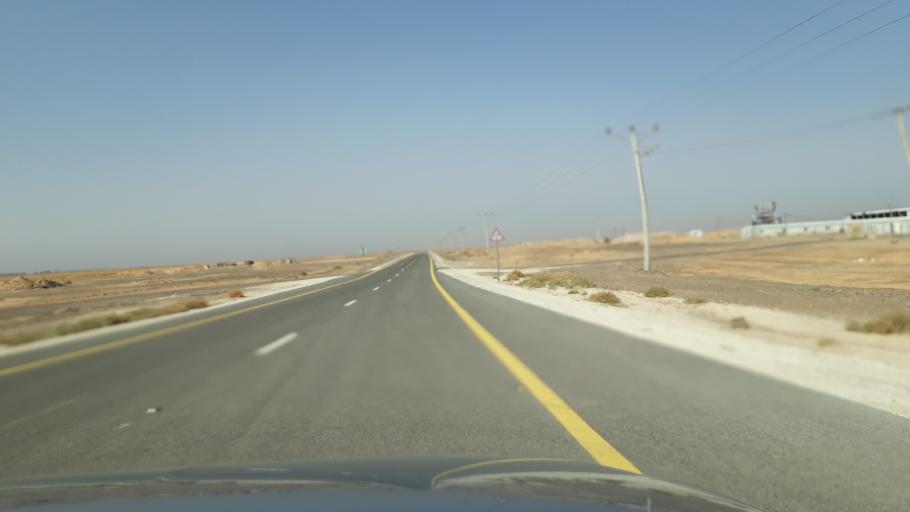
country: JO
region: Amman
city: Al Azraq ash Shamali
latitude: 31.7801
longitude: 36.7890
